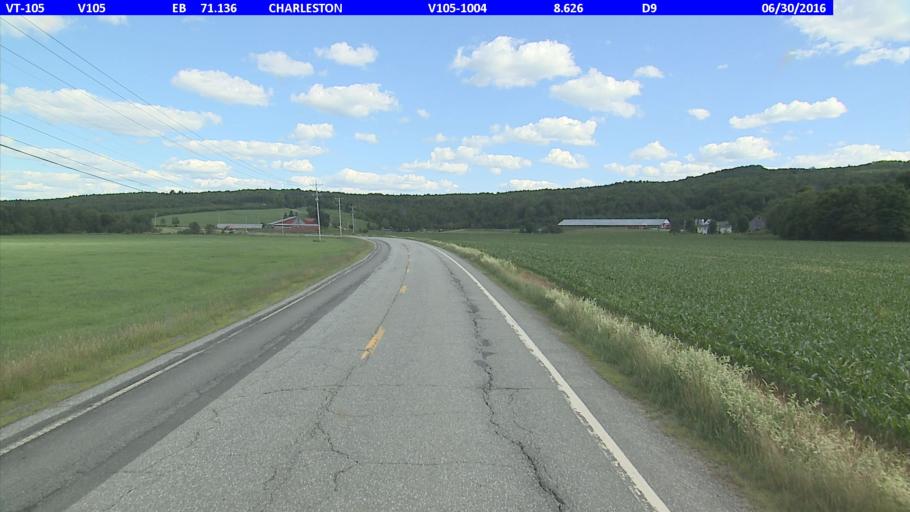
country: US
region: Vermont
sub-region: Orleans County
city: Newport
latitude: 44.8218
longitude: -71.9714
